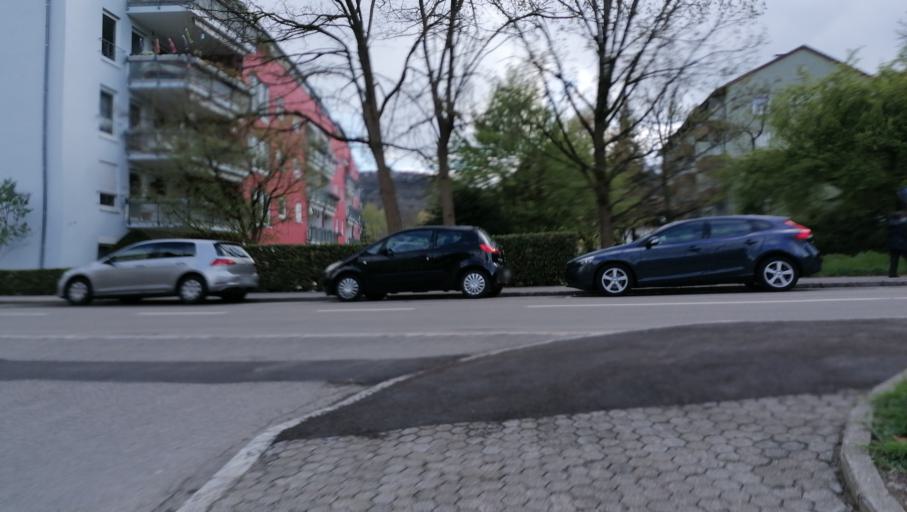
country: DE
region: Baden-Wuerttemberg
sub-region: Freiburg Region
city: Bad Sackingen
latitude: 47.5511
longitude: 7.9445
